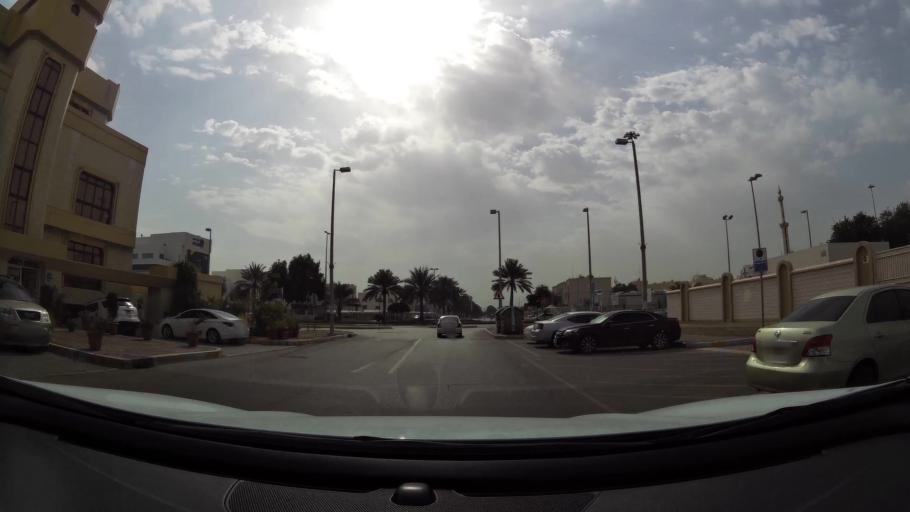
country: AE
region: Abu Dhabi
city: Abu Dhabi
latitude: 24.4598
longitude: 54.3840
